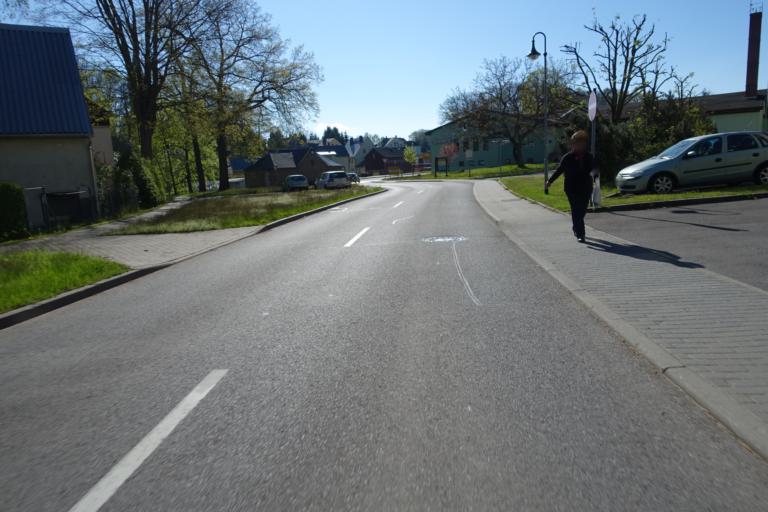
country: DE
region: Saxony
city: Lichtenberg
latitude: 50.8989
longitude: 13.4329
